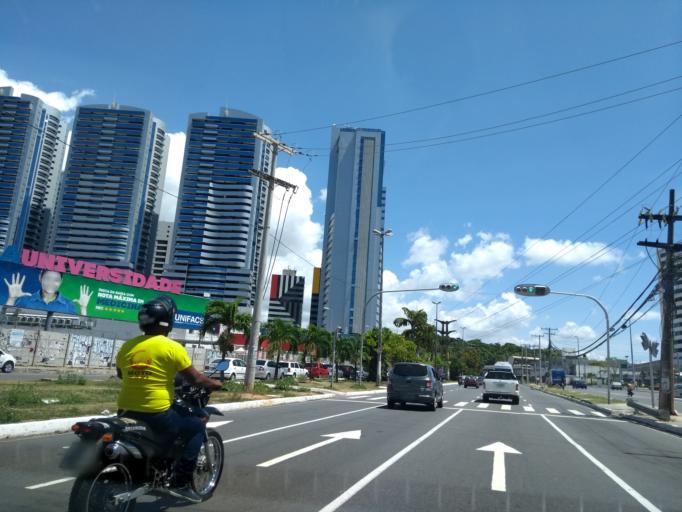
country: BR
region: Bahia
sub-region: Salvador
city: Salvador
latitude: -12.9828
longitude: -38.4507
